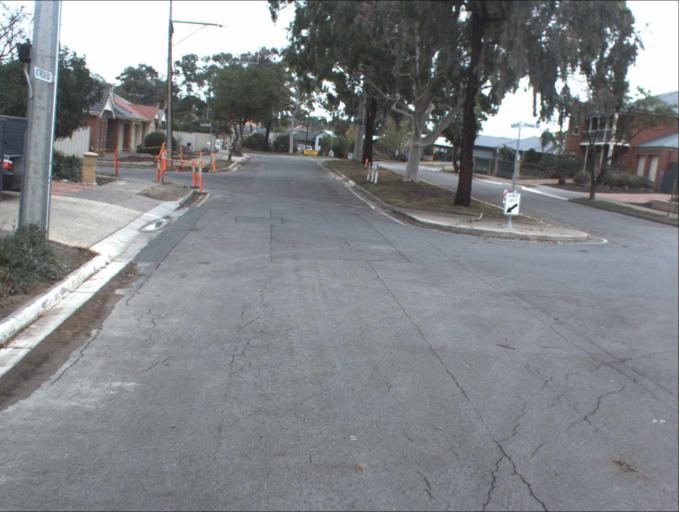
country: AU
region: South Australia
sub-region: Campbelltown
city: Paradise
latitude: -34.8709
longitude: 138.6524
